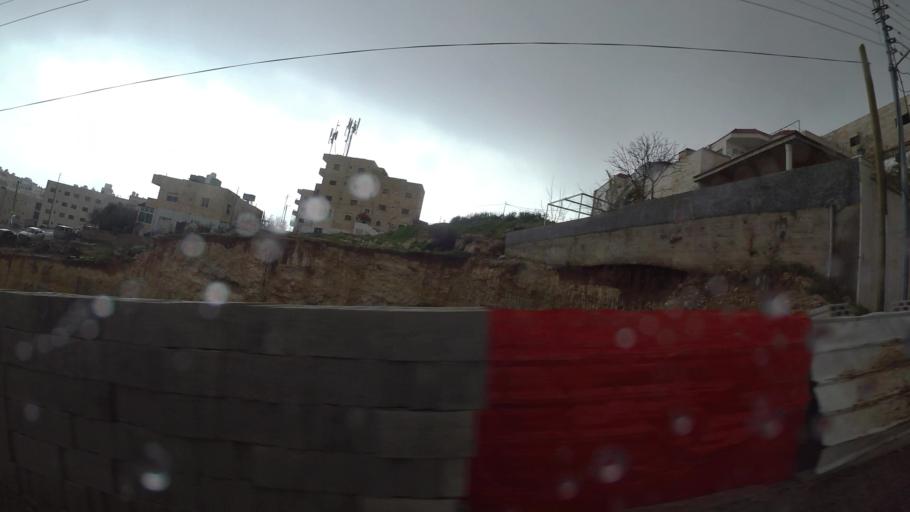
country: JO
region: Amman
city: Umm as Summaq
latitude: 31.8813
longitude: 35.8555
